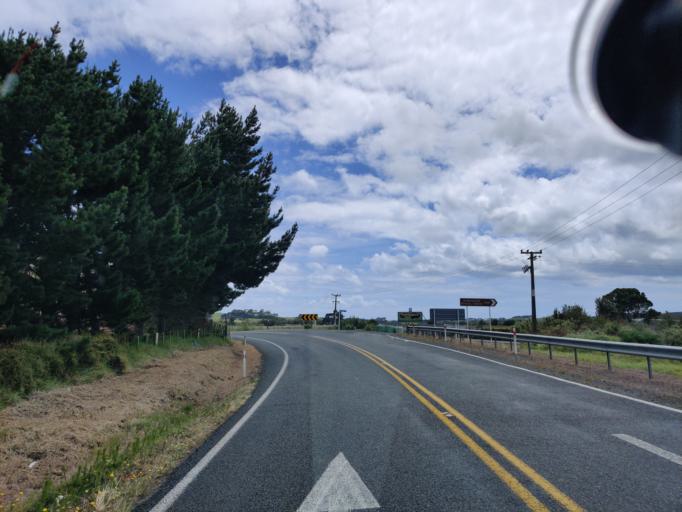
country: NZ
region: Northland
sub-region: Far North District
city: Kaitaia
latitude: -34.9805
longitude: 173.1933
